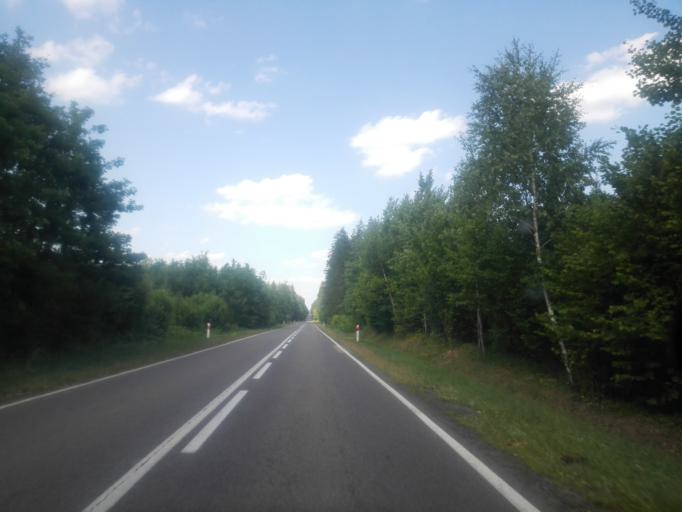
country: PL
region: Podlasie
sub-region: Powiat sejnenski
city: Sejny
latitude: 54.0141
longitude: 23.3331
